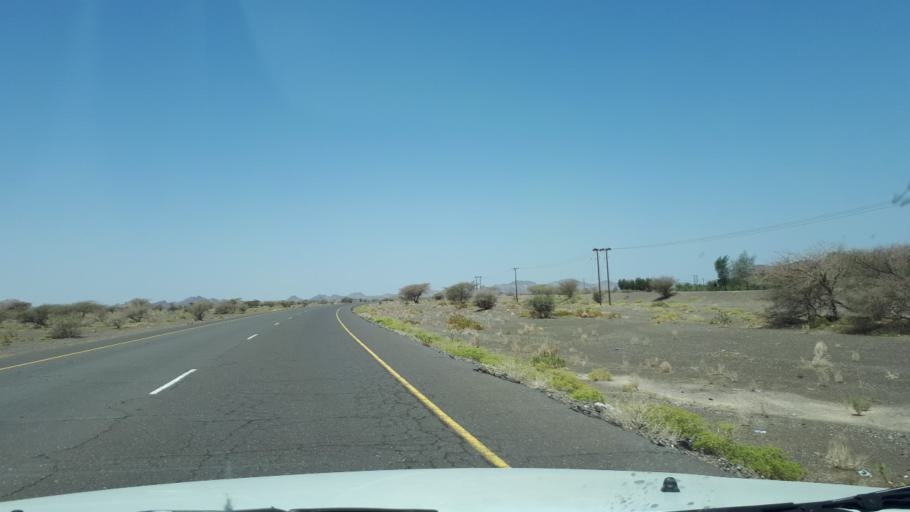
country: OM
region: Ash Sharqiyah
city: Ibra'
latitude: 22.6170
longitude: 58.4236
